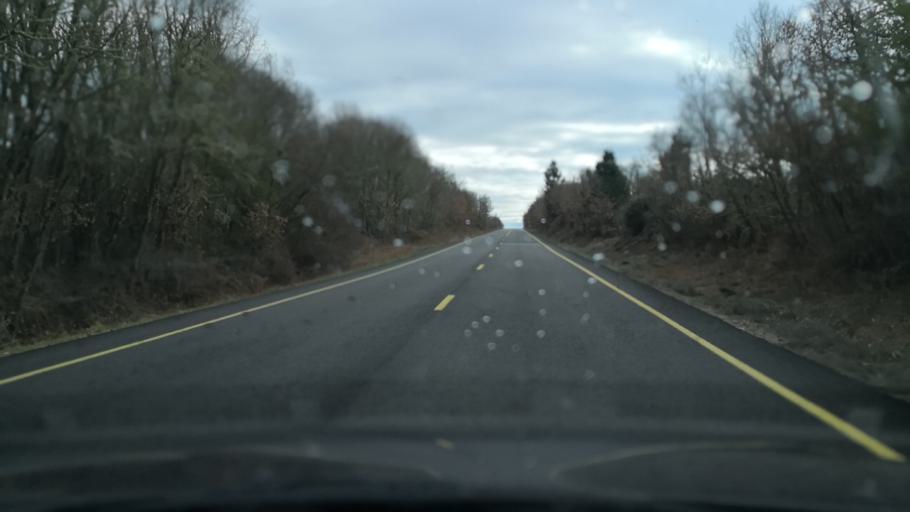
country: ES
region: Castille and Leon
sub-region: Provincia de Salamanca
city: Penaparda
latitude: 40.2887
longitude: -6.6677
